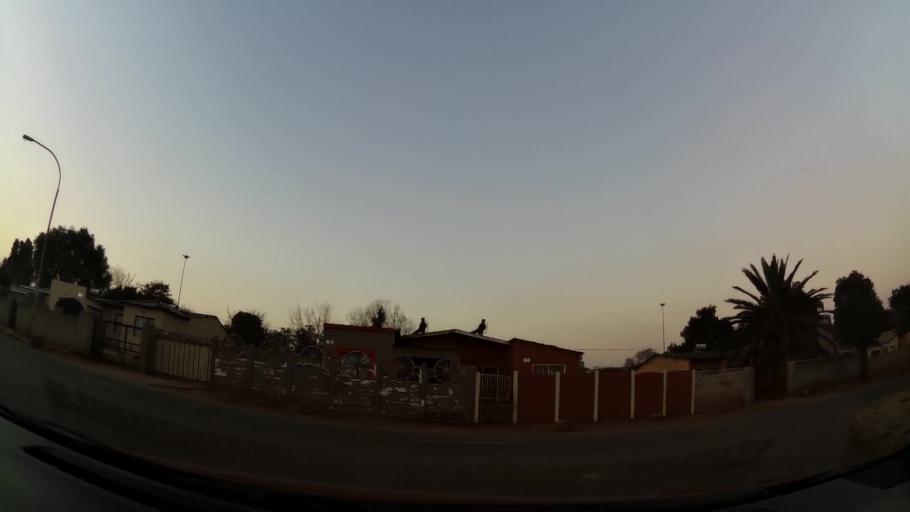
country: ZA
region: Gauteng
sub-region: City of Johannesburg Metropolitan Municipality
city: Soweto
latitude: -26.2899
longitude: 27.8755
